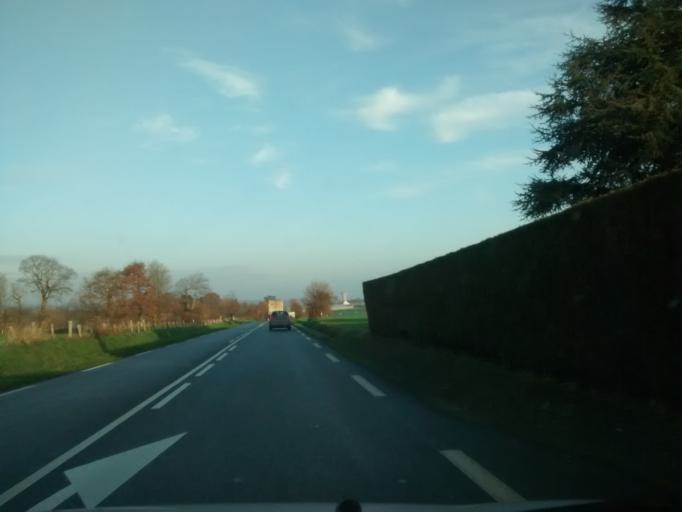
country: FR
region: Brittany
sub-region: Departement d'Ille-et-Vilaine
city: Tremblay
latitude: 48.4376
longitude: -1.4769
